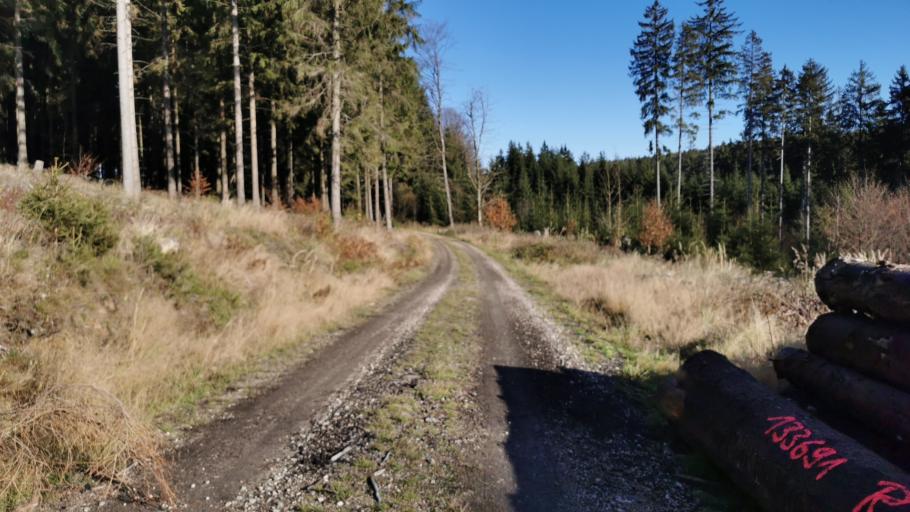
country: DE
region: Bavaria
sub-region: Upper Franconia
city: Reichenbach
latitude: 50.4504
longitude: 11.4320
